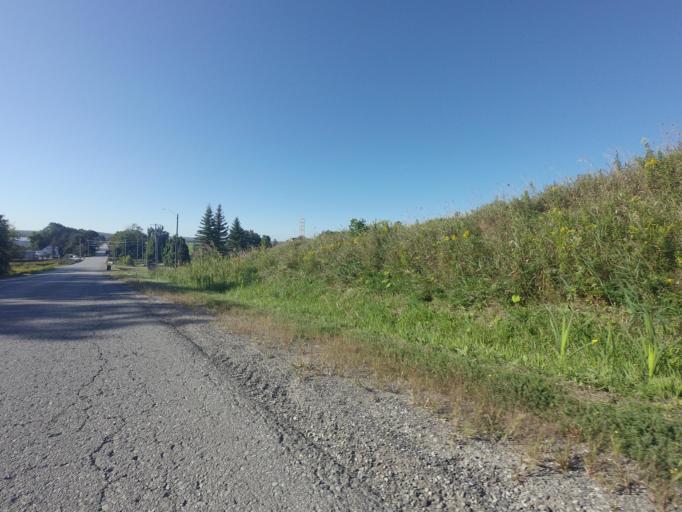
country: CA
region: Ontario
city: Bradford West Gwillimbury
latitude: 44.0453
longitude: -79.6252
